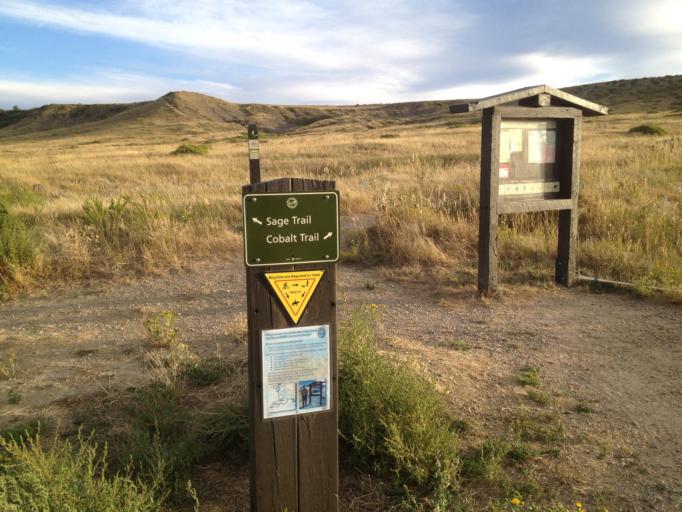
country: US
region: Colorado
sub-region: Boulder County
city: Boulder
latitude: 40.0797
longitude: -105.2626
